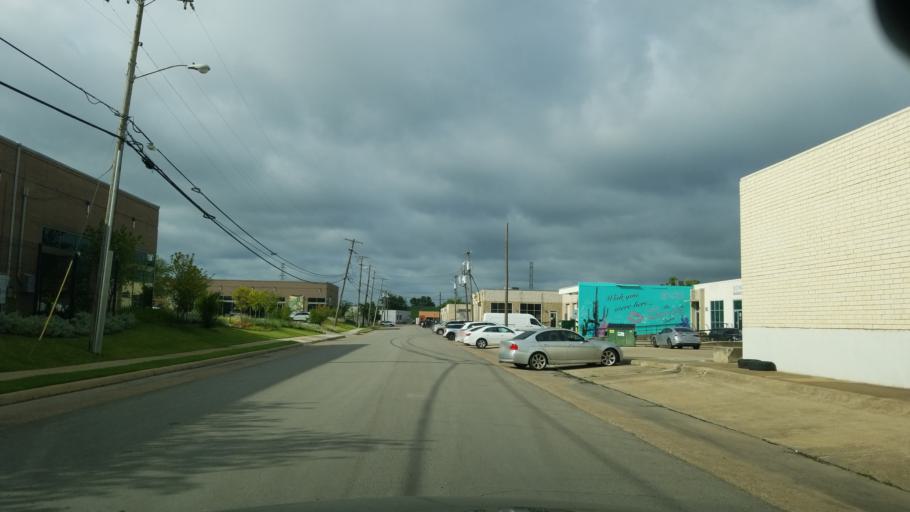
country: US
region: Texas
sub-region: Dallas County
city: Dallas
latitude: 32.7951
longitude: -96.8304
